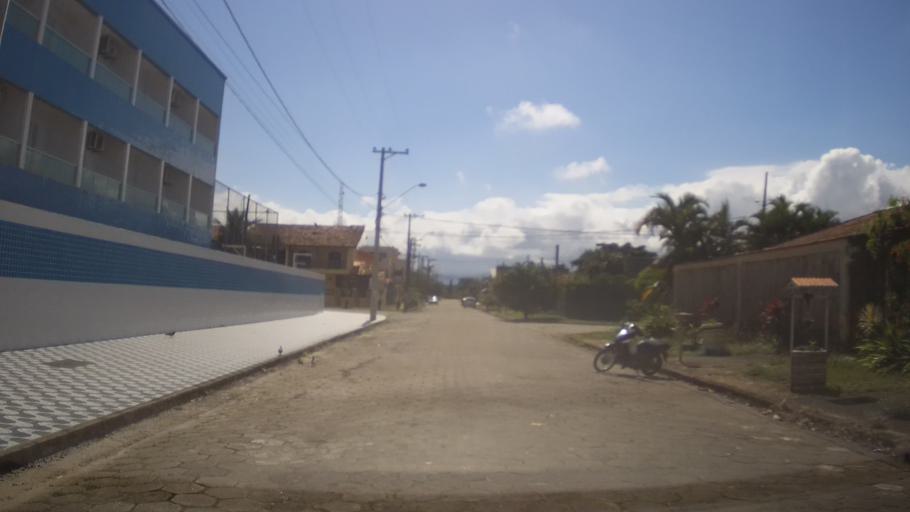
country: BR
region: Sao Paulo
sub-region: Itanhaem
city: Itanhaem
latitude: -24.1715
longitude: -46.7616
